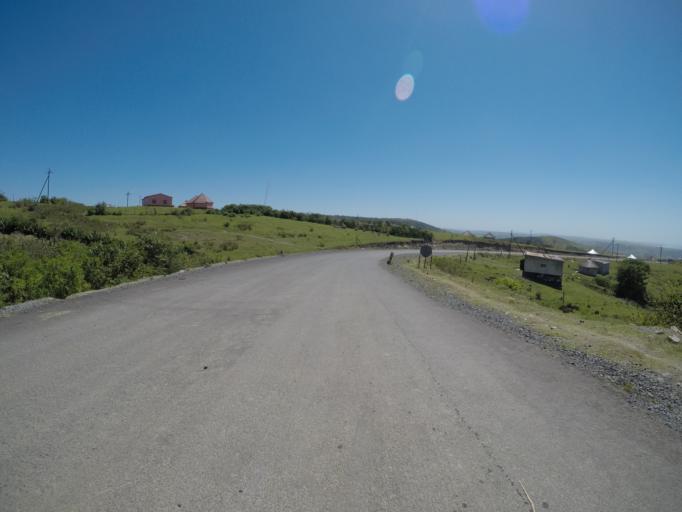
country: ZA
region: Eastern Cape
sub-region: OR Tambo District Municipality
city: Libode
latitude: -31.9979
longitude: 29.1228
